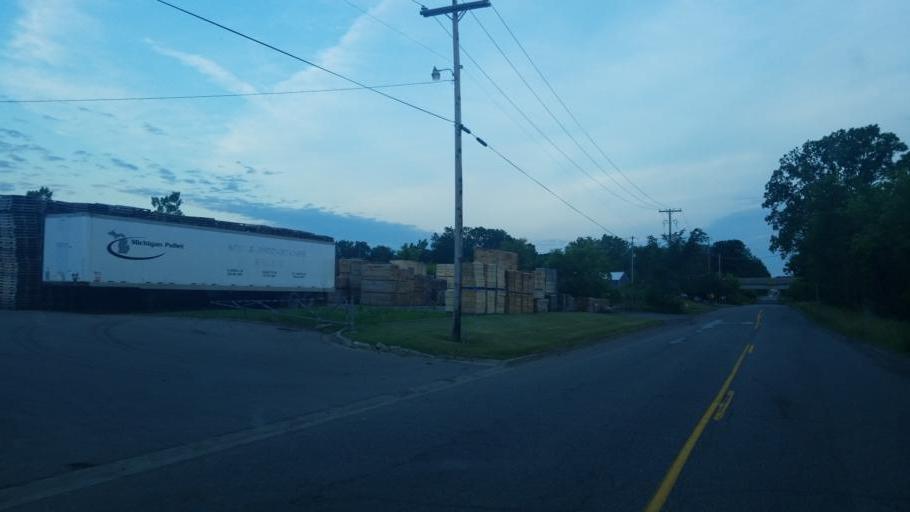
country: US
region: Michigan
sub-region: Eaton County
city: Charlotte
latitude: 42.5821
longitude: -84.8133
